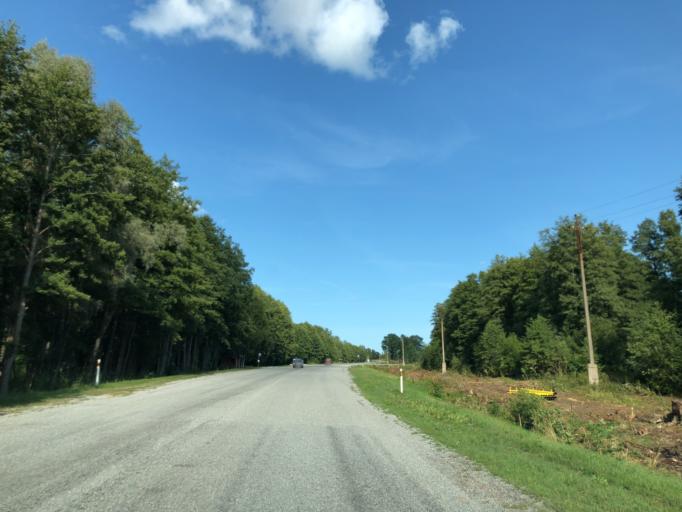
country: EE
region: Hiiumaa
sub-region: Kaerdla linn
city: Kardla
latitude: 58.8228
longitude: 22.7450
